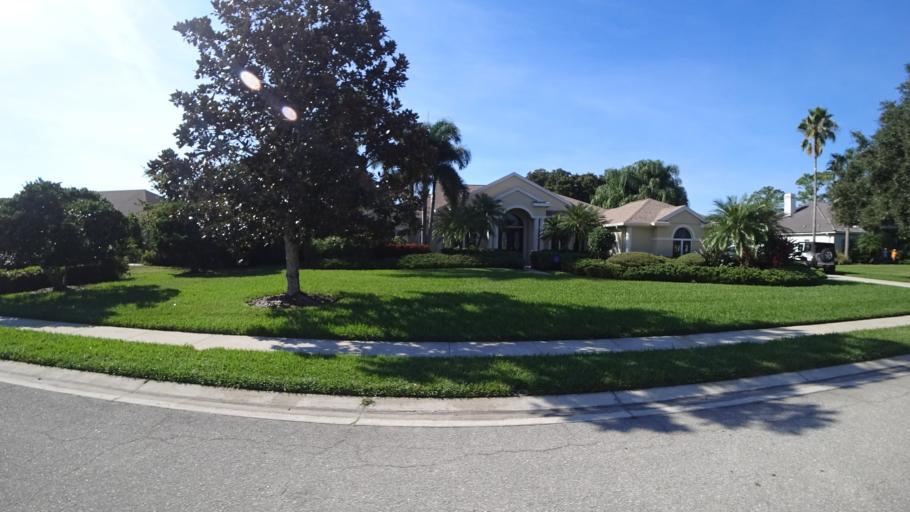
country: US
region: Florida
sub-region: Sarasota County
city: The Meadows
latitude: 27.4133
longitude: -82.4445
